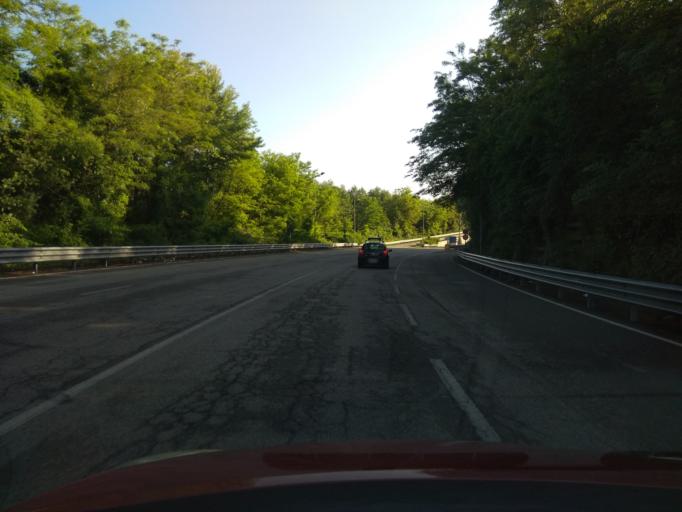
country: IT
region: Piedmont
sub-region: Provincia di Biella
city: Quaregna
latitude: 45.5755
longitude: 8.1689
